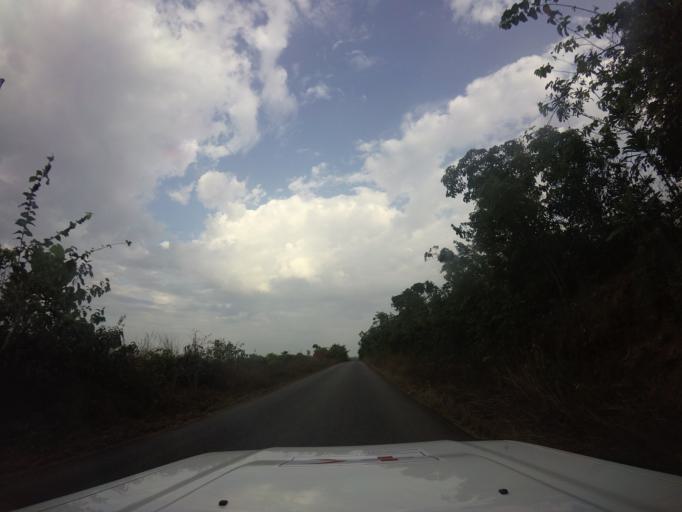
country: LR
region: Bomi
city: Tubmanburg
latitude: 6.7105
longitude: -10.9334
